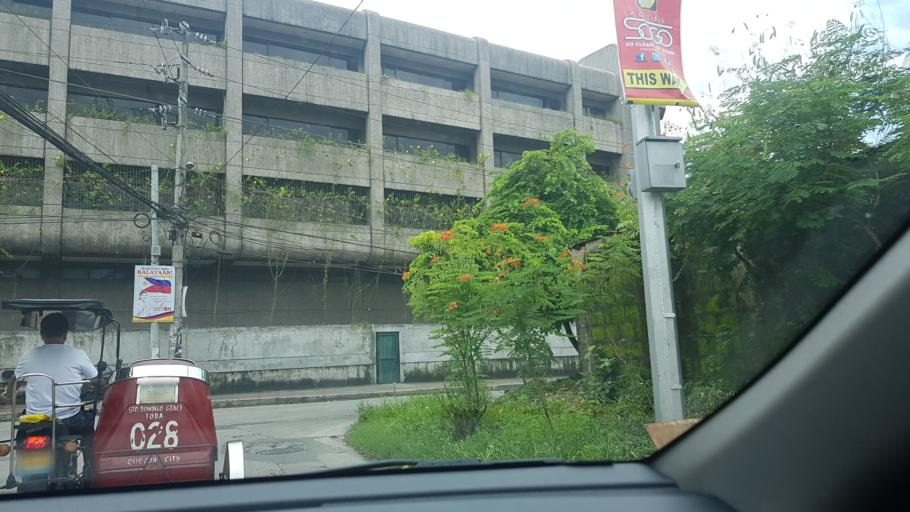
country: PH
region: Calabarzon
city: Del Monte
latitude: 14.6464
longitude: 121.0058
